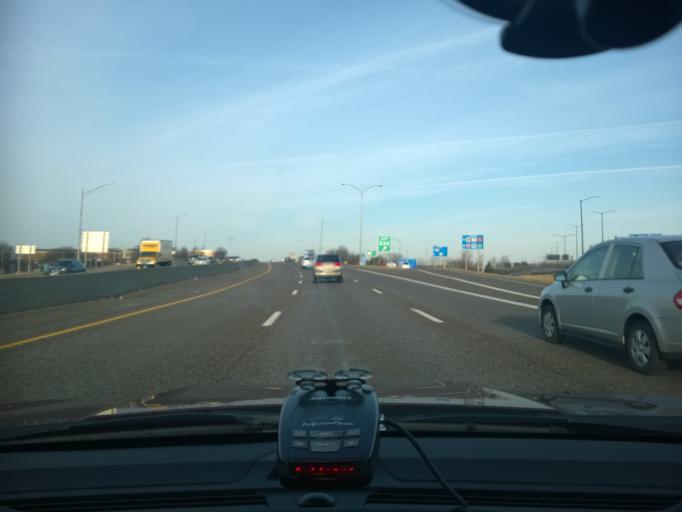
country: US
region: Missouri
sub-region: Saint Louis County
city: Woodson Terrace
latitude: 38.7393
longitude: -90.3643
